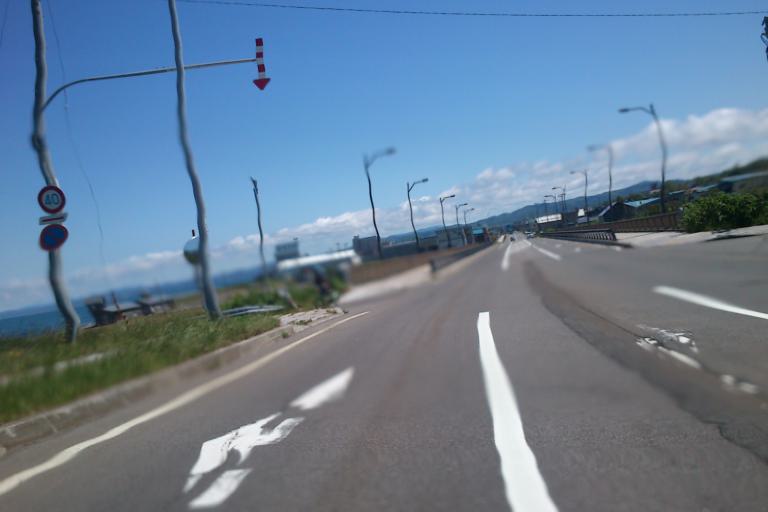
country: JP
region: Hokkaido
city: Rumoi
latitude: 43.8542
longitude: 141.5099
